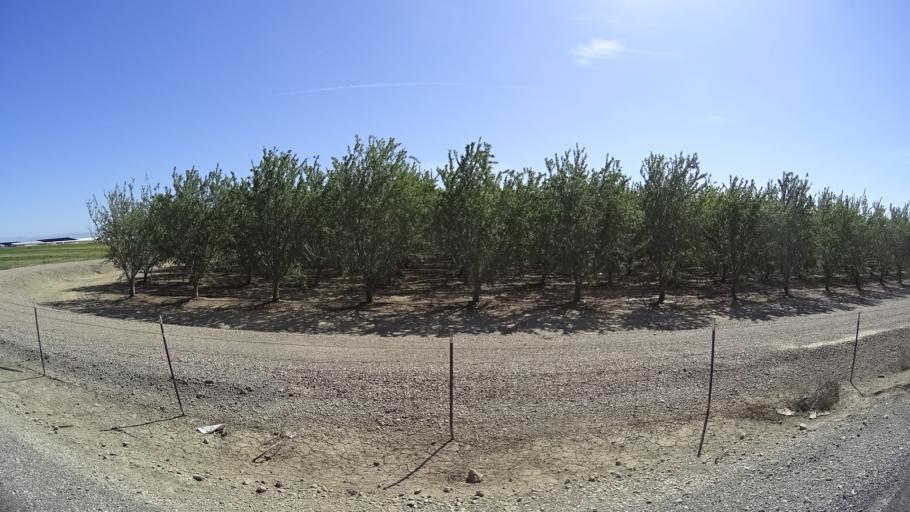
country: US
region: California
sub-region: Glenn County
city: Hamilton City
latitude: 39.6665
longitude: -122.1034
